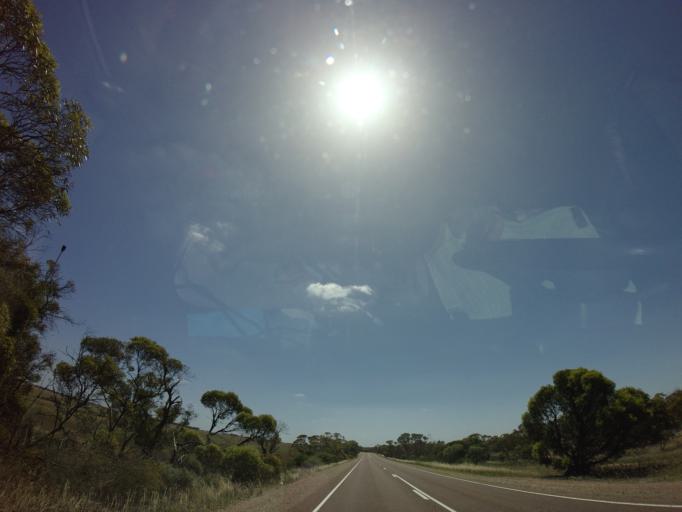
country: AU
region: South Australia
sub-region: Kimba
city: Caralue
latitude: -33.2126
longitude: 136.3536
